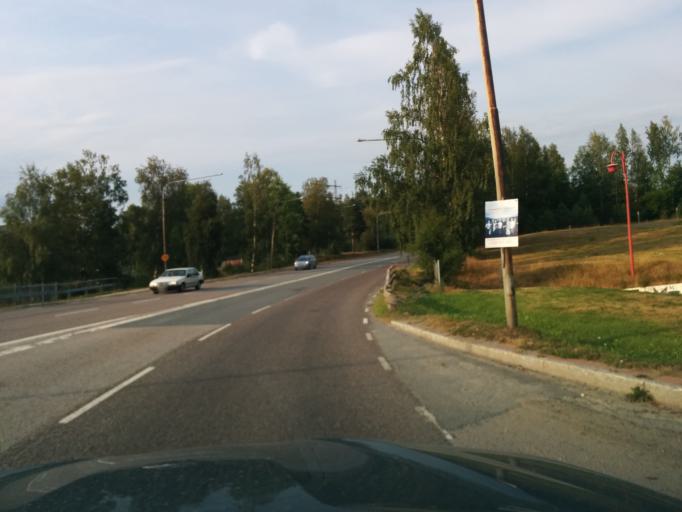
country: SE
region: Vaesternorrland
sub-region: OErnskoeldsviks Kommun
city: Ornskoldsvik
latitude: 63.2728
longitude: 18.6928
